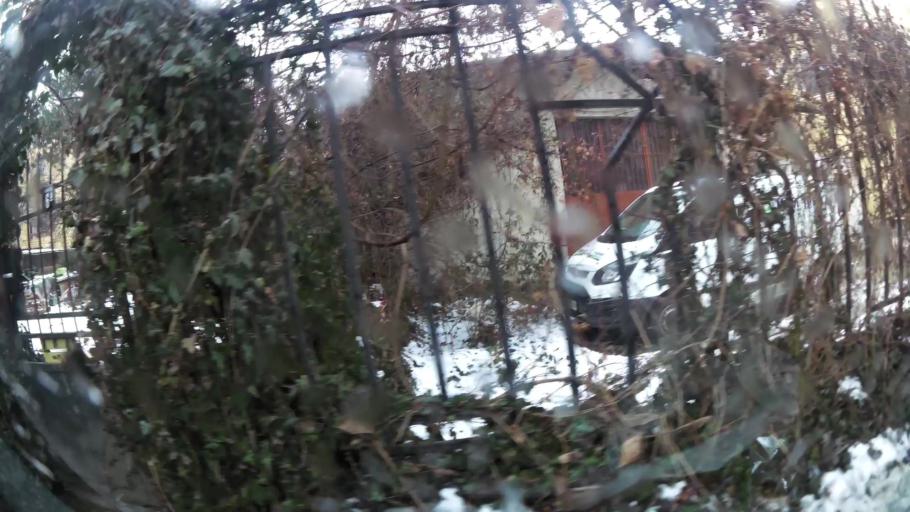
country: BG
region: Sofia-Capital
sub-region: Stolichna Obshtina
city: Sofia
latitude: 42.6645
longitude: 23.2823
